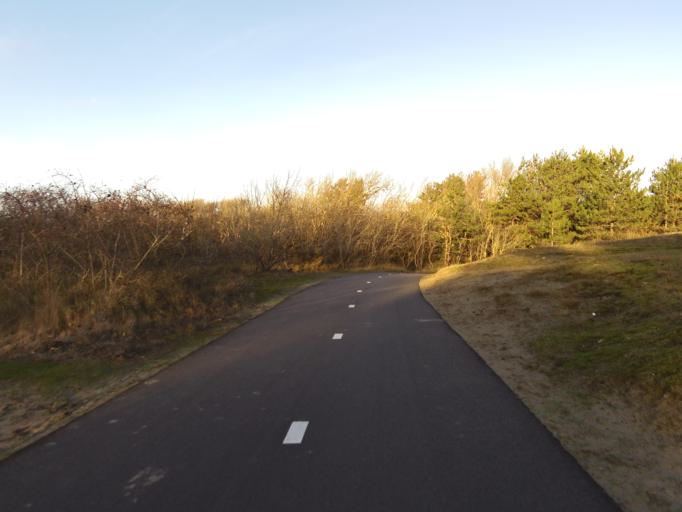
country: NL
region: South Holland
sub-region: Gemeente Noordwijk
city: Noordwijk-Binnen
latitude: 52.2612
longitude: 4.4524
